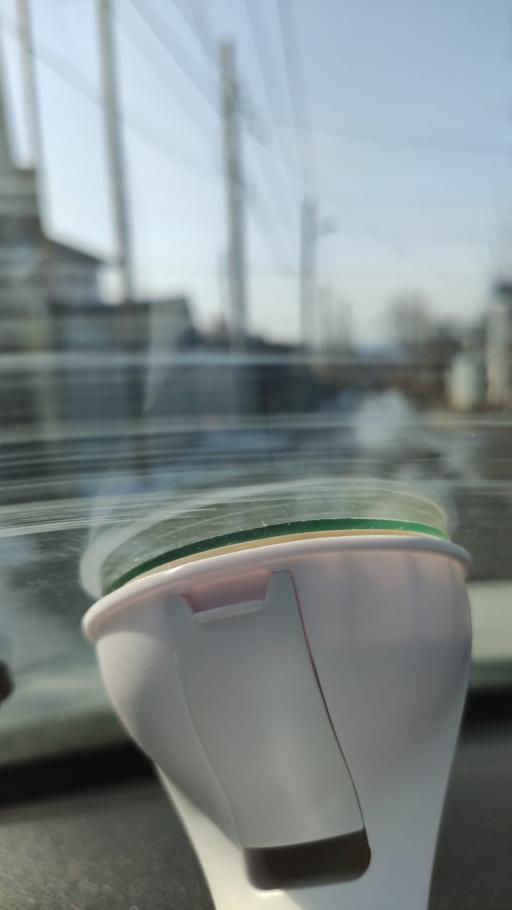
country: RU
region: Samara
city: Samara
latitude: 53.2719
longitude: 50.2142
